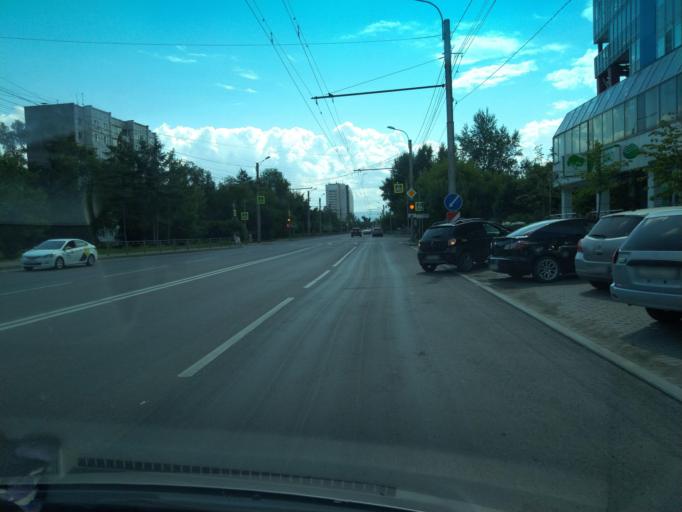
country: RU
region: Krasnoyarskiy
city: Solnechnyy
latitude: 56.0463
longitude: 92.9413
